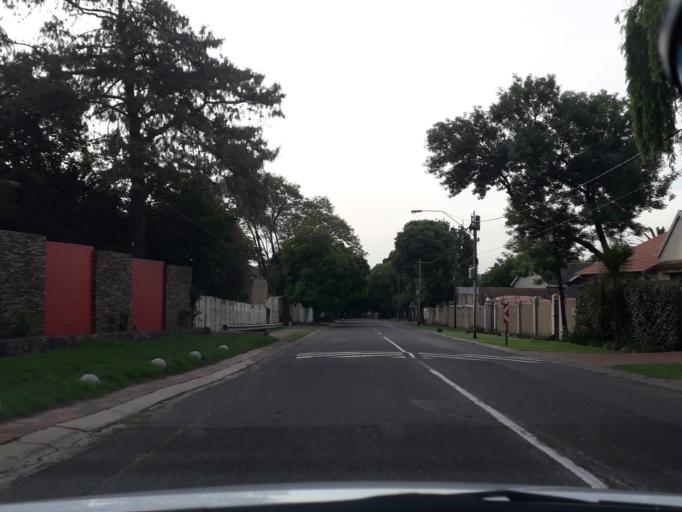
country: ZA
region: Gauteng
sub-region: City of Johannesburg Metropolitan Municipality
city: Johannesburg
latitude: -26.1325
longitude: 28.0798
